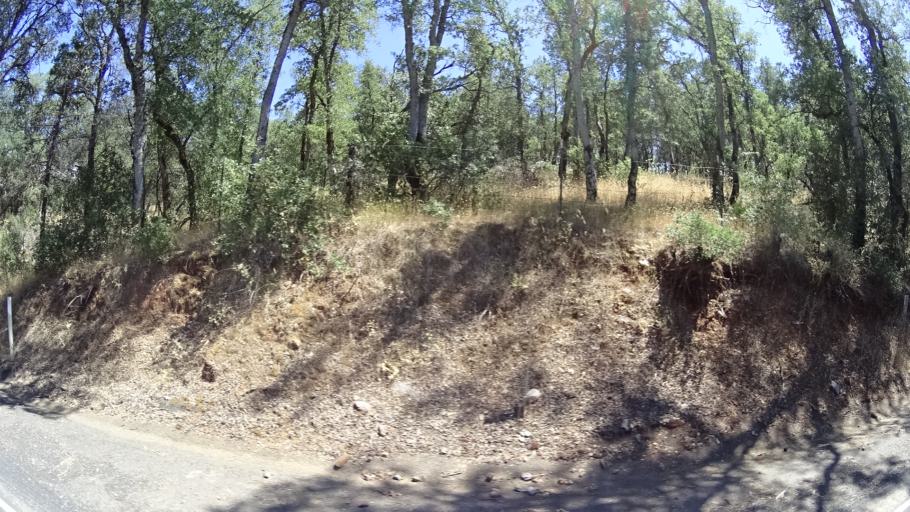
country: US
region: California
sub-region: Calaveras County
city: Forest Meadows
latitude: 38.2124
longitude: -120.4642
